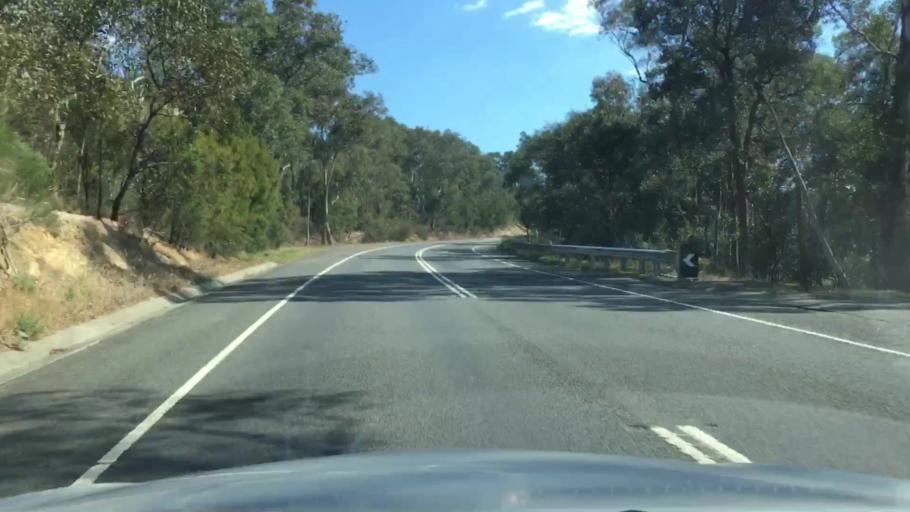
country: AU
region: Victoria
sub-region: Nillumbik
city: North Warrandyte
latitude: -37.6784
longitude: 145.2438
